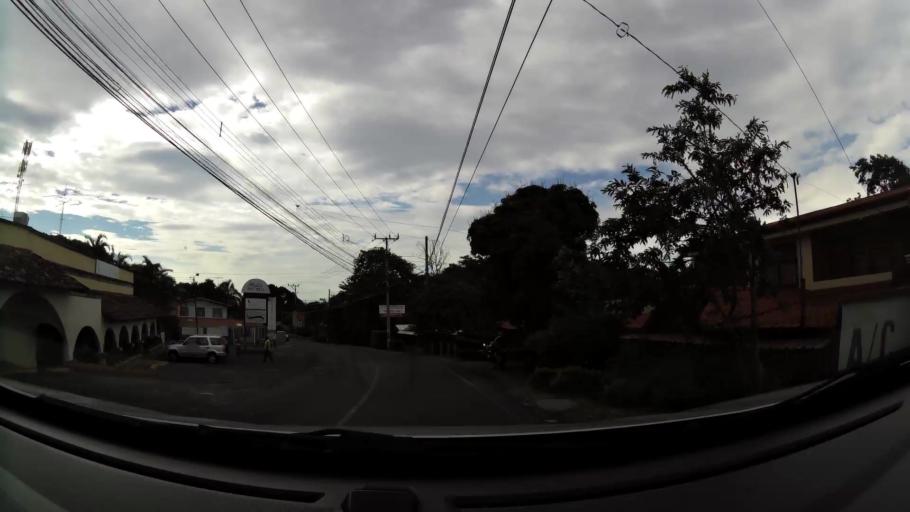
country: CR
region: San Jose
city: Santa Ana
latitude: 9.9304
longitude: -84.1752
